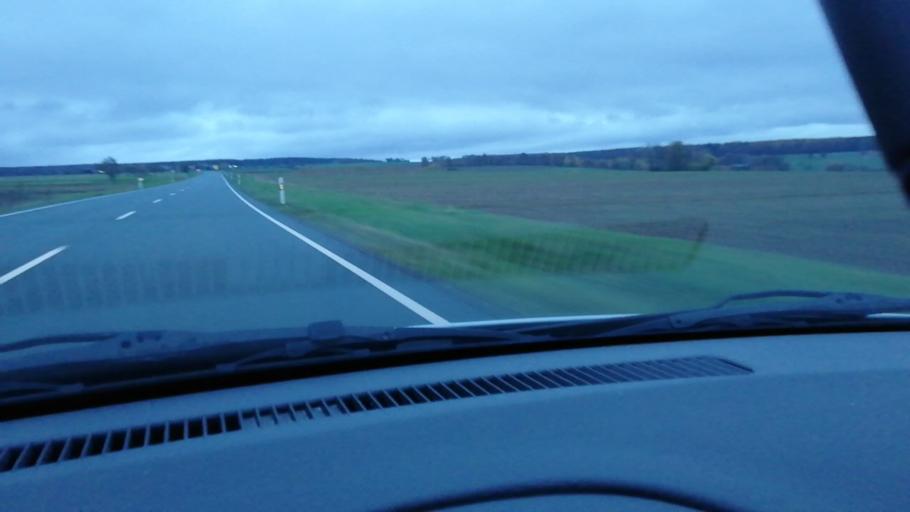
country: DE
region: Bavaria
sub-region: Regierungsbezirk Unterfranken
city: Esselbach
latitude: 49.8636
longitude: 9.5101
